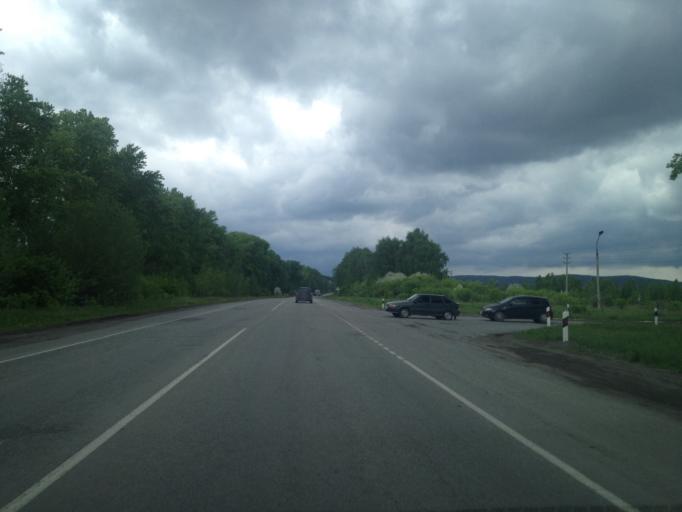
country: RU
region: Sverdlovsk
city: Aramil
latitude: 56.6949
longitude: 60.7791
